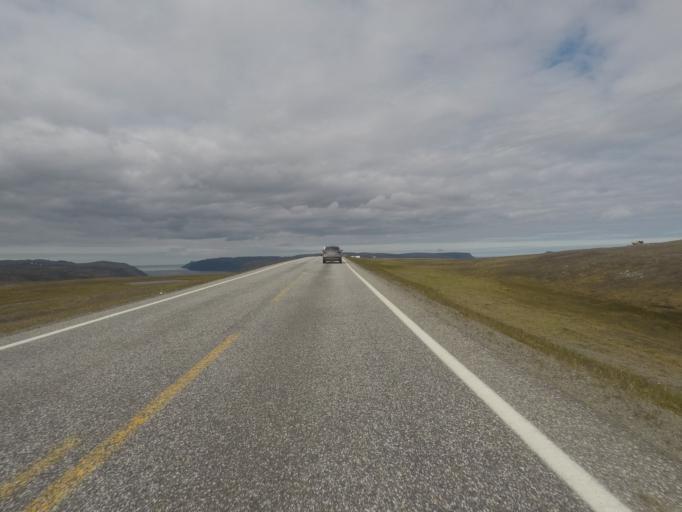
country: NO
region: Finnmark Fylke
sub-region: Nordkapp
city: Honningsvag
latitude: 71.0543
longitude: 25.7649
